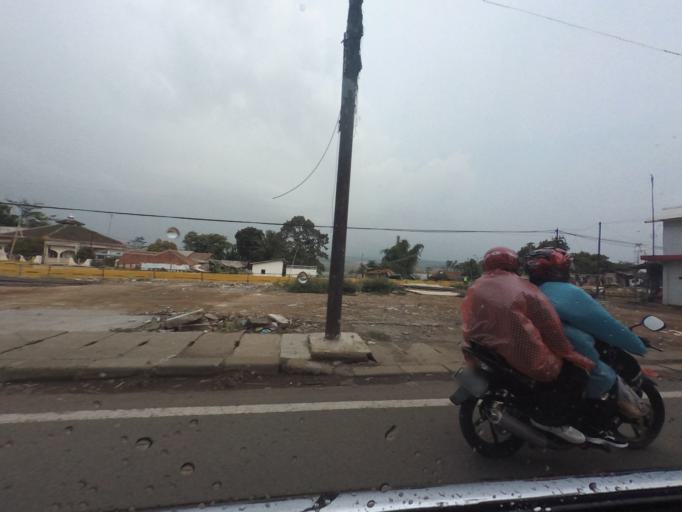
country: ID
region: West Java
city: Cicurug
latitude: -6.7552
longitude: 106.7994
